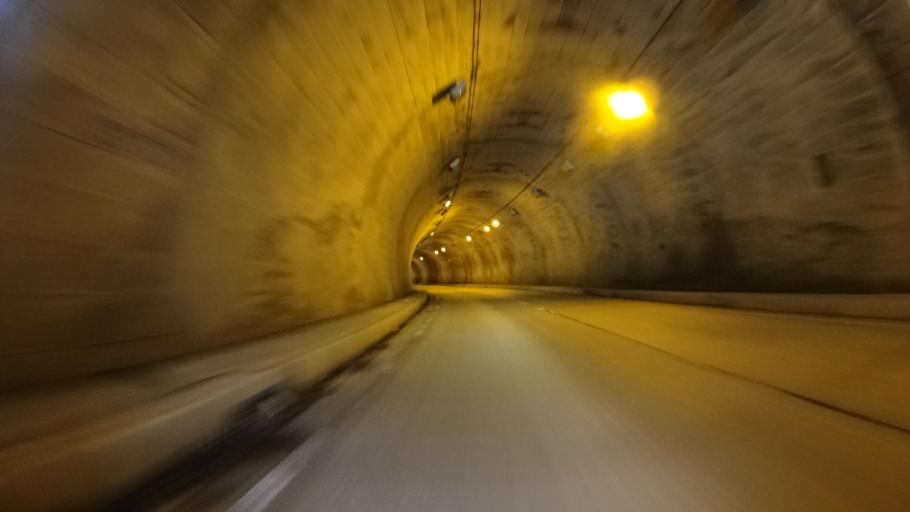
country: JP
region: Yamanashi
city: Nirasaki
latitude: 35.8696
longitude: 138.5054
